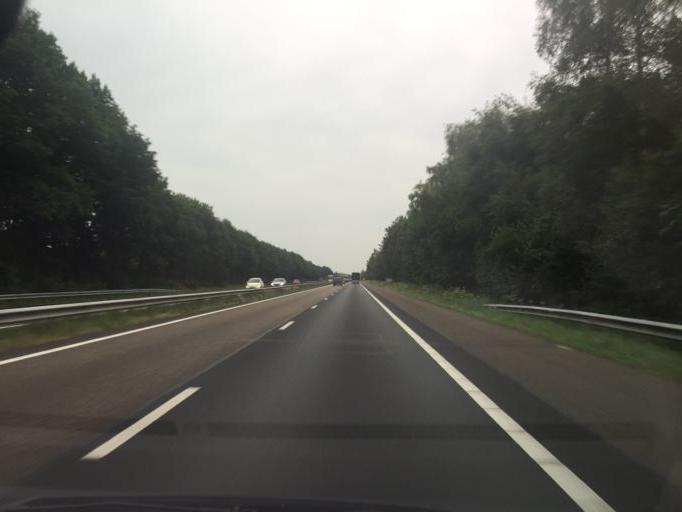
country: NL
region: North Brabant
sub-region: Gemeente Geldrop-Mierlo
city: Geldrop
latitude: 51.4124
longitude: 5.5794
